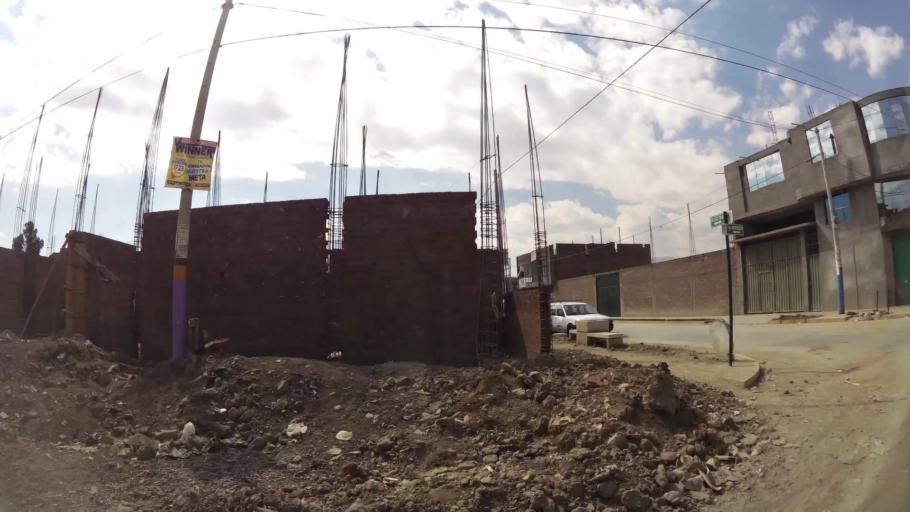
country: PE
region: Junin
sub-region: Provincia de Huancayo
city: Huancayo
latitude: -12.0940
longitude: -75.2029
